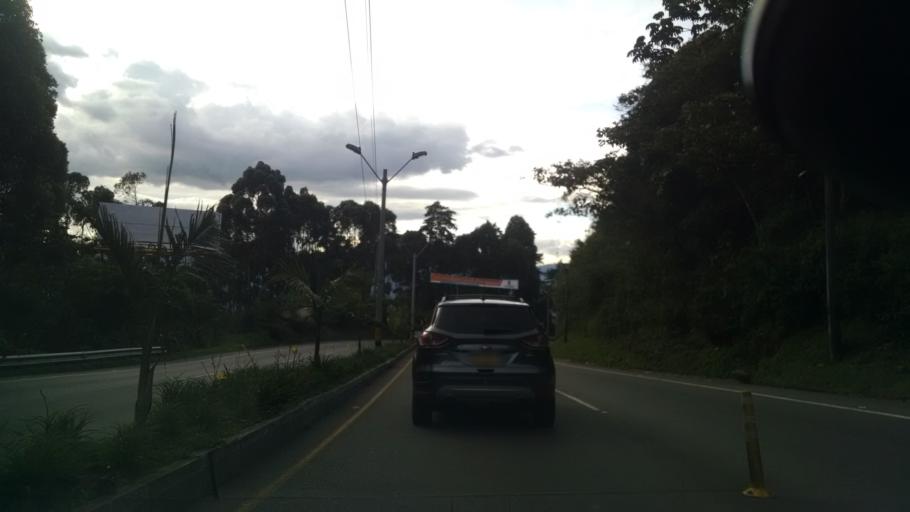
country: CO
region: Antioquia
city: Envigado
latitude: 6.1815
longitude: -75.5443
